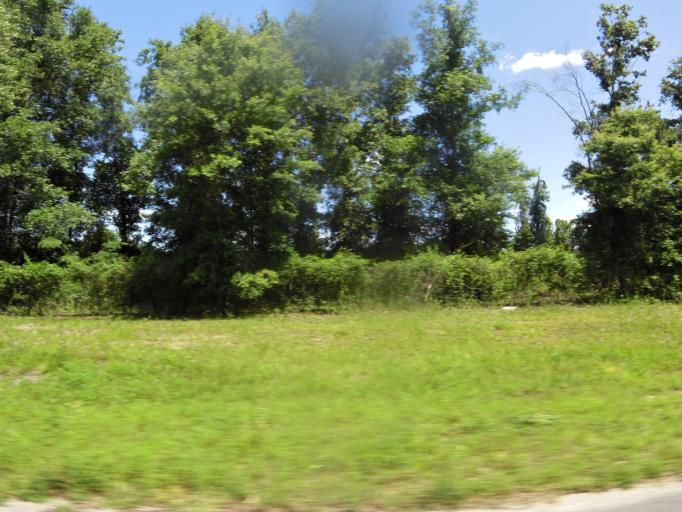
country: US
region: Florida
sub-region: Union County
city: Lake Butler
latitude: 30.0341
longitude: -82.2185
